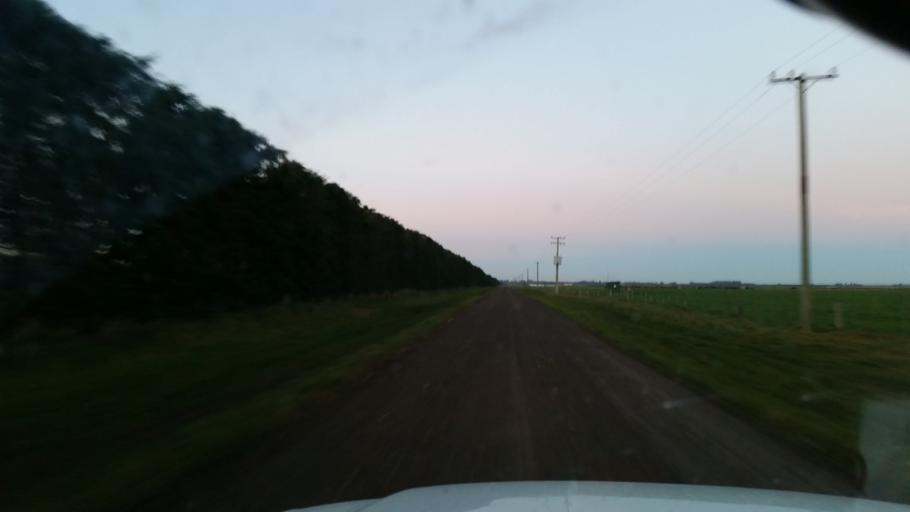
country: NZ
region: Canterbury
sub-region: Ashburton District
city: Tinwald
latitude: -43.9363
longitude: 171.5766
